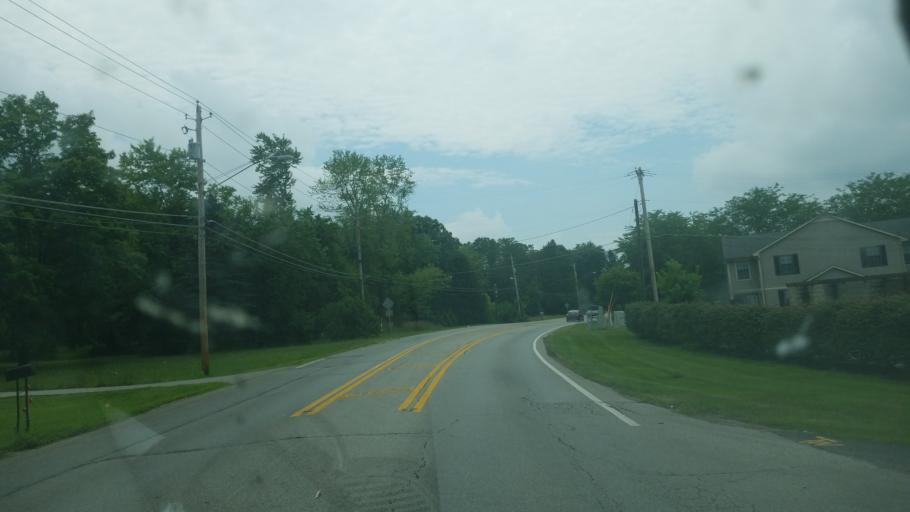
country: US
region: Ohio
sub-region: Franklin County
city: Reynoldsburg
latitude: 39.9622
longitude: -82.7936
